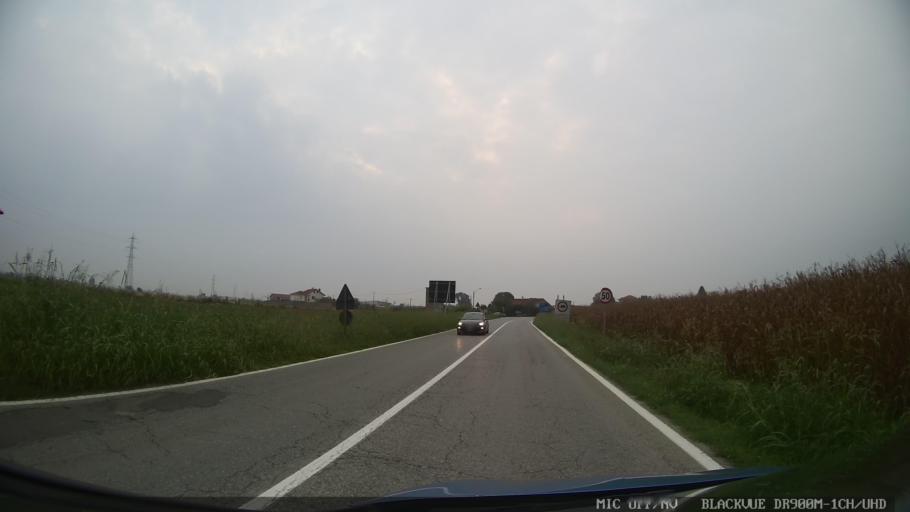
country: IT
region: Piedmont
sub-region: Provincia di Torino
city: Carmagnola
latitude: 44.8706
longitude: 7.7102
